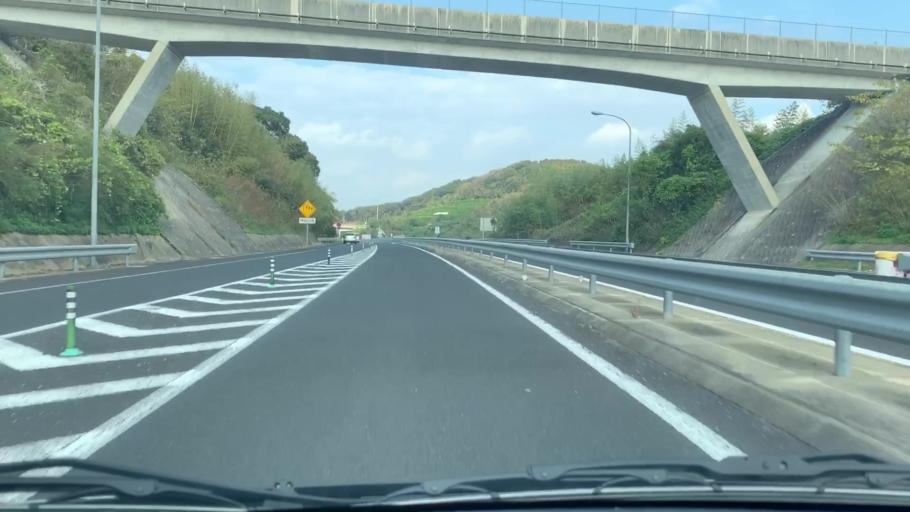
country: JP
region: Nagasaki
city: Sasebo
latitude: 33.0448
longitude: 129.7492
